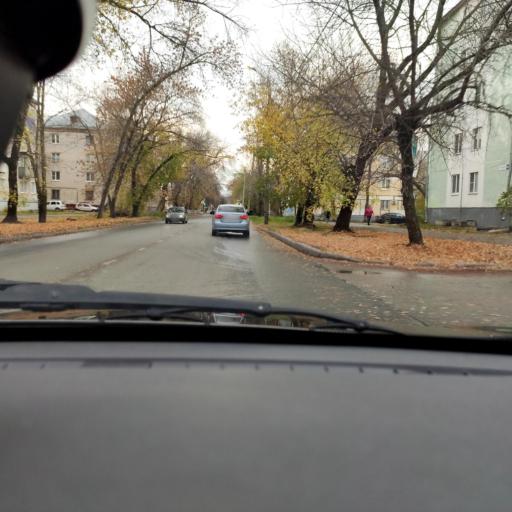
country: RU
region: Samara
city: Tol'yatti
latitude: 53.5065
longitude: 49.4074
